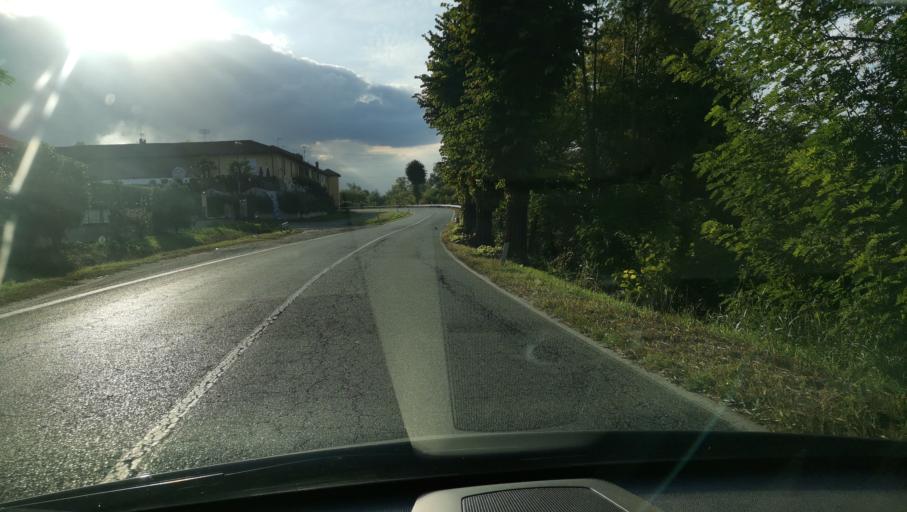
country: IT
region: Piedmont
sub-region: Provincia di Torino
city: Castagneto Po
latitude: 45.1762
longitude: 7.8822
